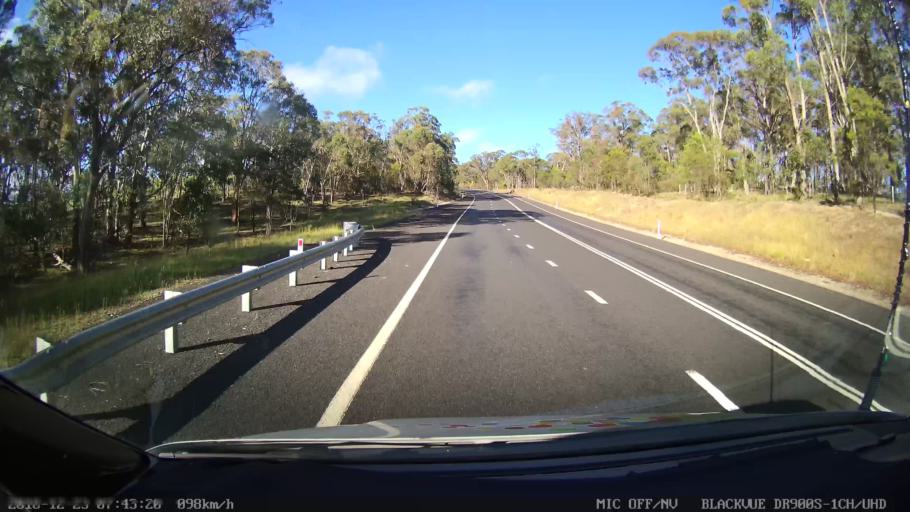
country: AU
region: New South Wales
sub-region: Armidale Dumaresq
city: Enmore
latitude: -30.5215
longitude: 151.9657
